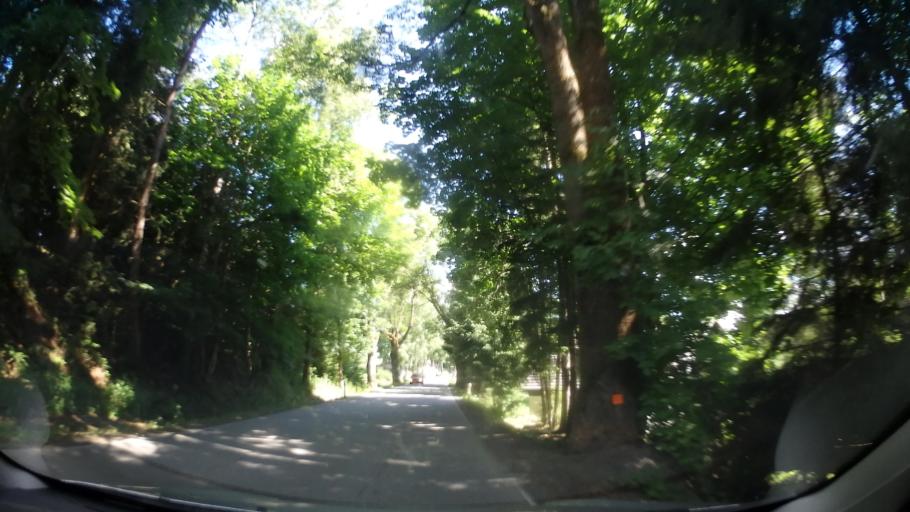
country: CZ
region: Vysocina
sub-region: Okres Zd'ar nad Sazavou
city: Nove Mesto na Morave
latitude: 49.6330
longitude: 16.1173
